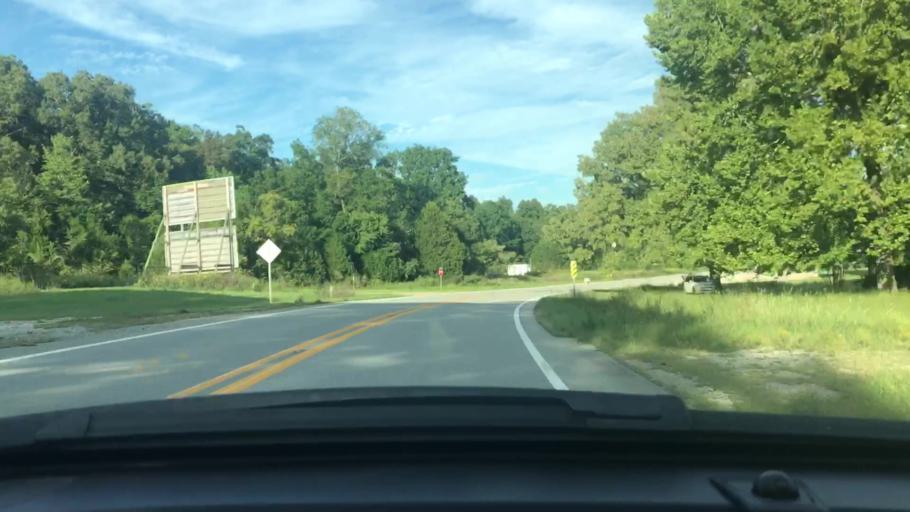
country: US
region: Arkansas
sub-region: Sharp County
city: Cherokee Village
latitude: 36.2743
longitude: -91.3516
